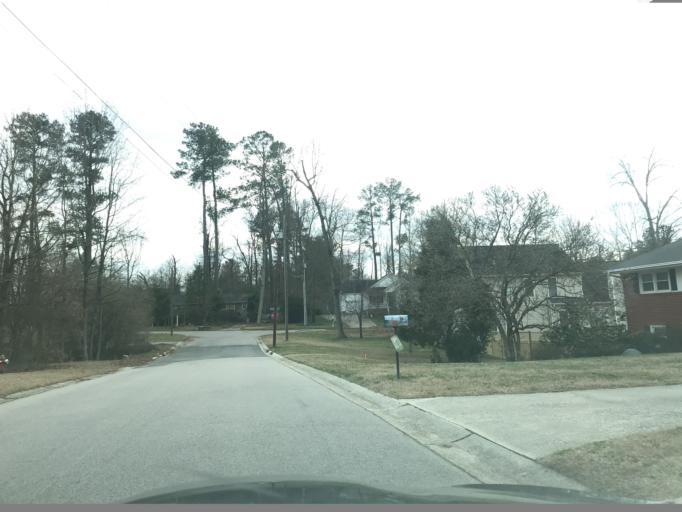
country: US
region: North Carolina
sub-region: Wake County
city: Raleigh
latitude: 35.8226
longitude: -78.5779
